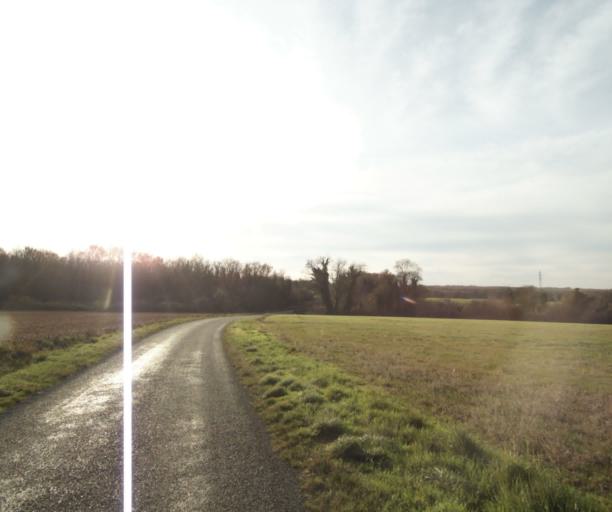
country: FR
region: Poitou-Charentes
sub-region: Departement de la Charente-Maritime
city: Fontcouverte
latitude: 45.8184
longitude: -0.5837
